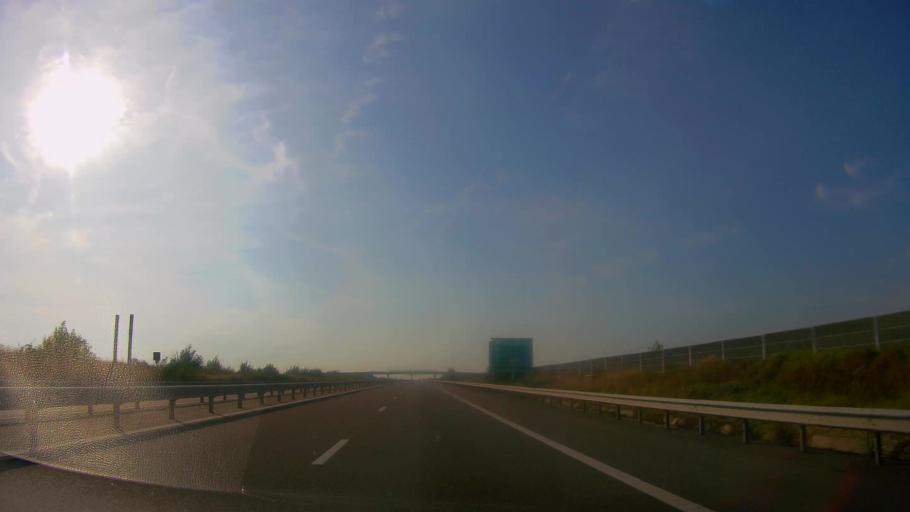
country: RO
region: Prahova
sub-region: Comuna Olari
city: Olari
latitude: 44.8077
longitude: 26.2286
